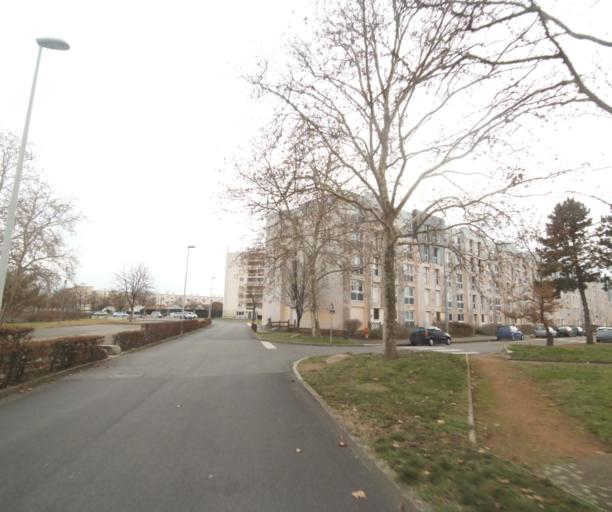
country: FR
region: Rhone-Alpes
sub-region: Departement de la Loire
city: Le Coteau
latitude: 46.0604
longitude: 4.0912
